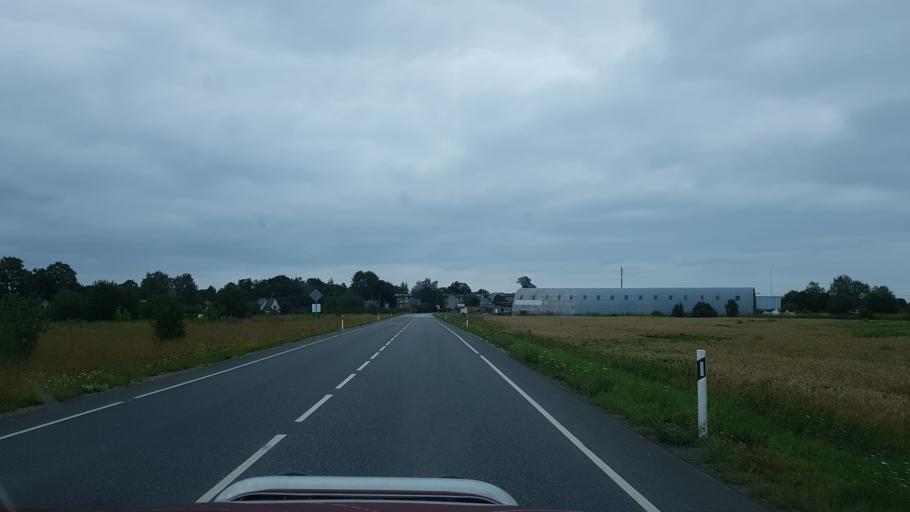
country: EE
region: Ida-Virumaa
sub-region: Johvi vald
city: Johvi
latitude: 59.3315
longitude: 27.3767
